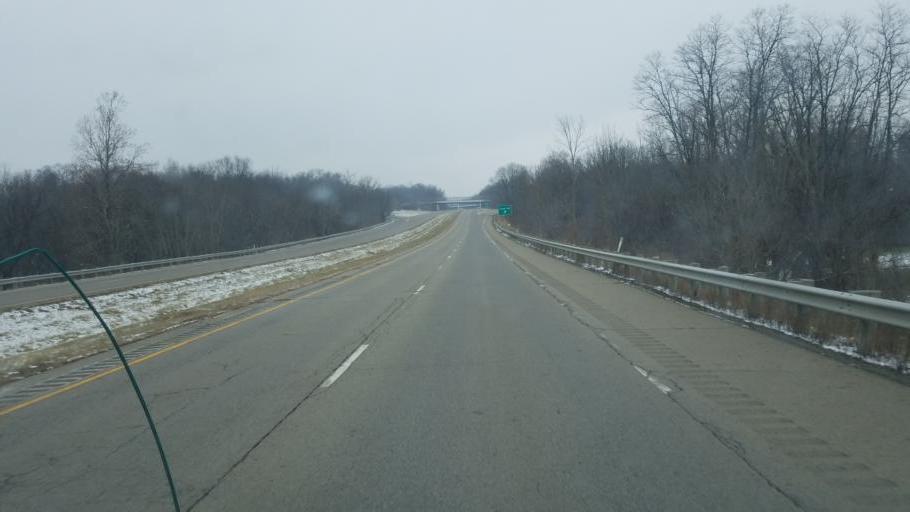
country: US
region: Ohio
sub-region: Richland County
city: Mansfield
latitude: 40.7285
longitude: -82.5050
